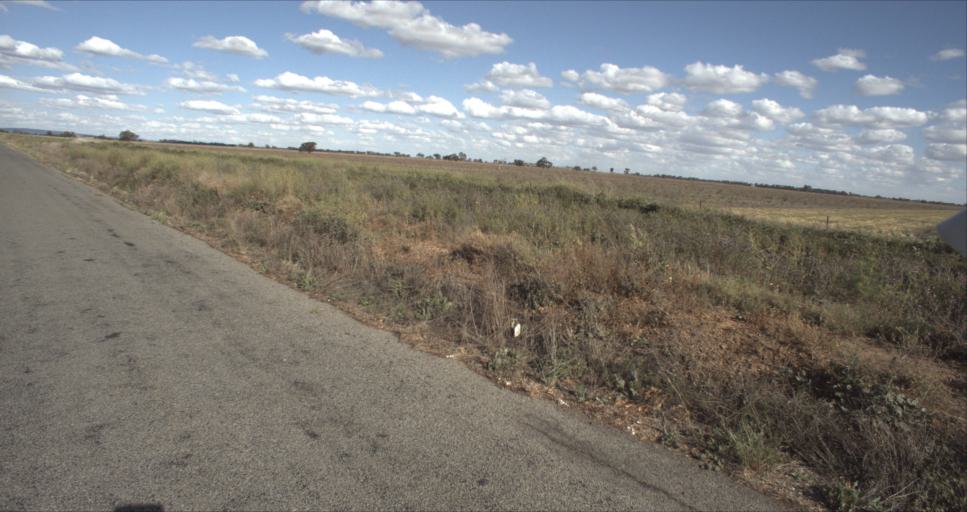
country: AU
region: New South Wales
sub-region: Leeton
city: Leeton
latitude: -34.4422
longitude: 146.2392
